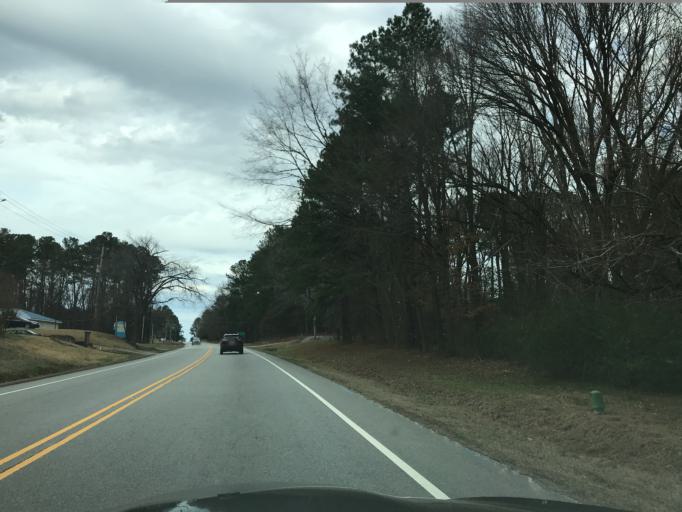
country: US
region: North Carolina
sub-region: Franklin County
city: Louisburg
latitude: 36.1098
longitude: -78.2917
